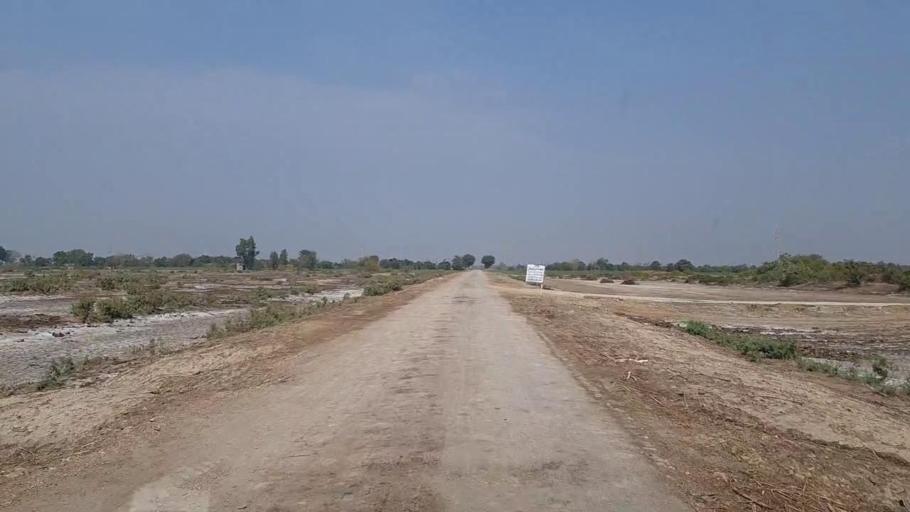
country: PK
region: Sindh
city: Mirwah Gorchani
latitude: 25.3248
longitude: 69.0615
